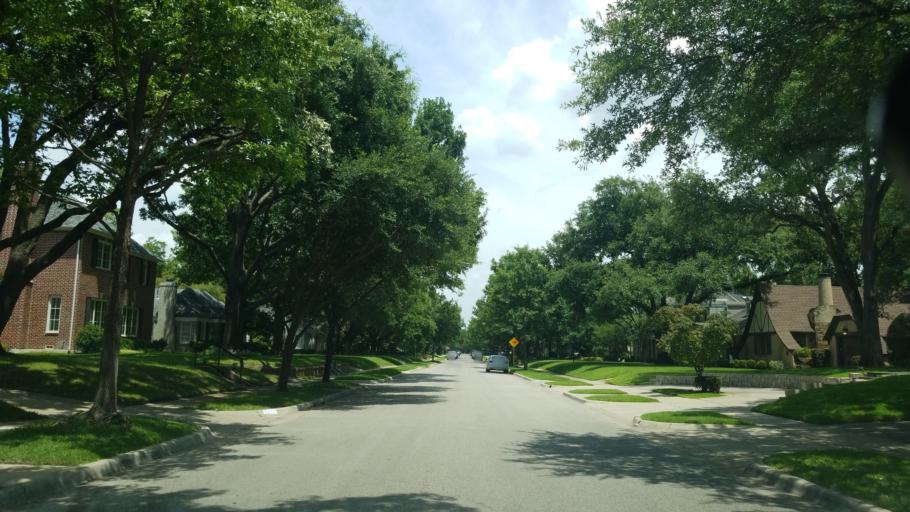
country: US
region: Texas
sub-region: Dallas County
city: University Park
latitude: 32.8540
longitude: -96.8079
